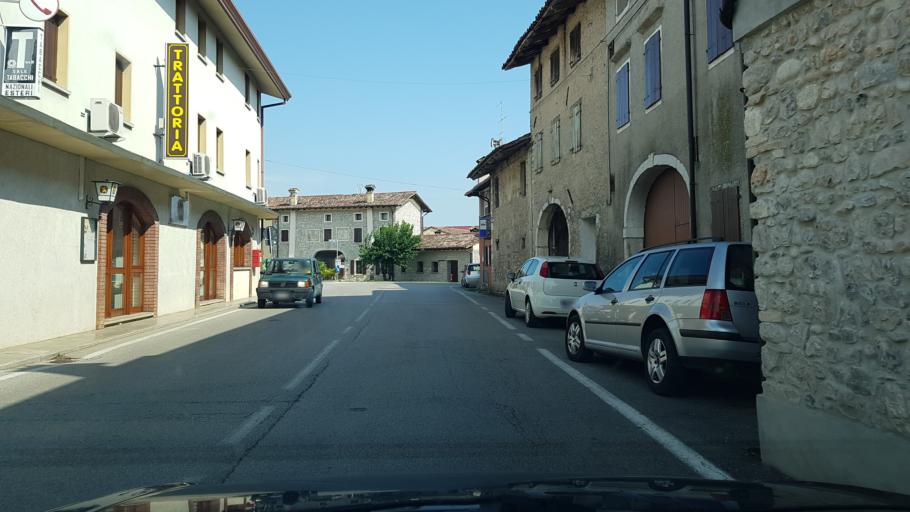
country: IT
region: Friuli Venezia Giulia
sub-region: Provincia di Pordenone
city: San Quirino
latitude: 46.0542
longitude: 12.6685
